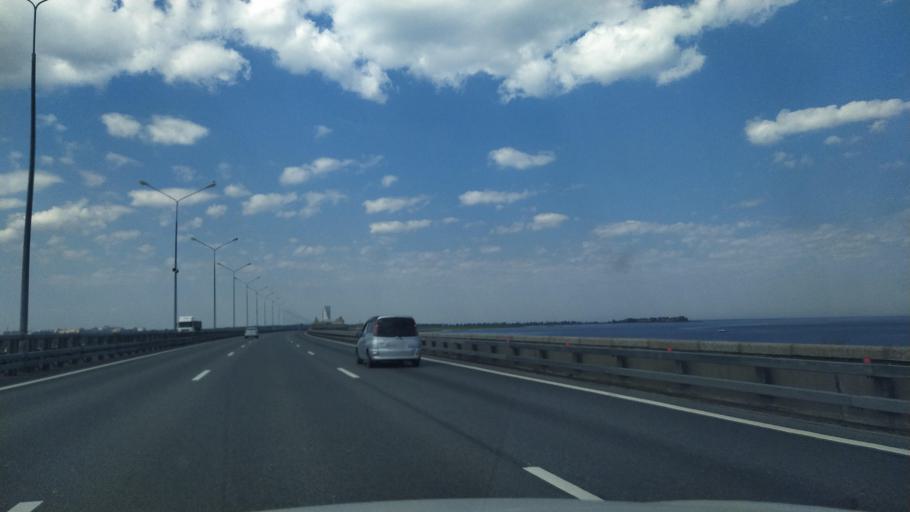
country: RU
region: St.-Petersburg
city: Kronshtadt
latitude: 60.0218
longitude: 29.7901
